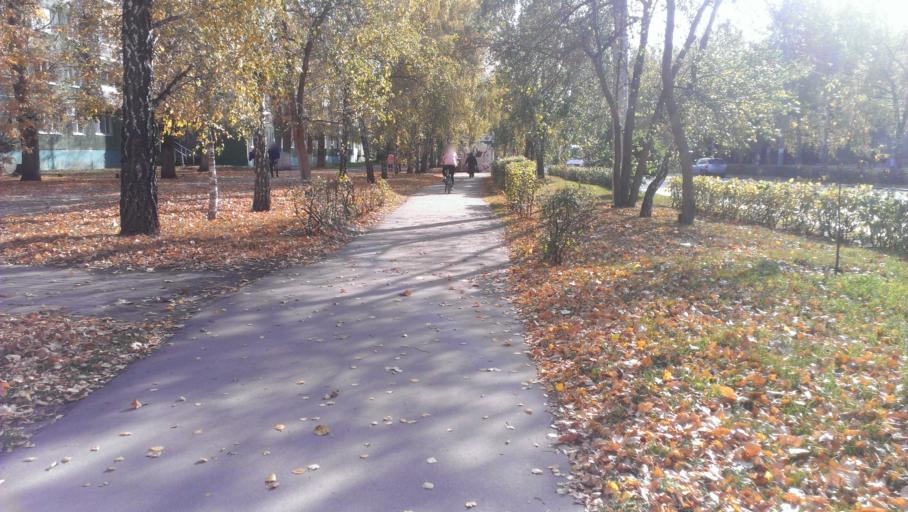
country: RU
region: Altai Krai
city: Novosilikatnyy
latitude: 53.3543
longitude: 83.6845
